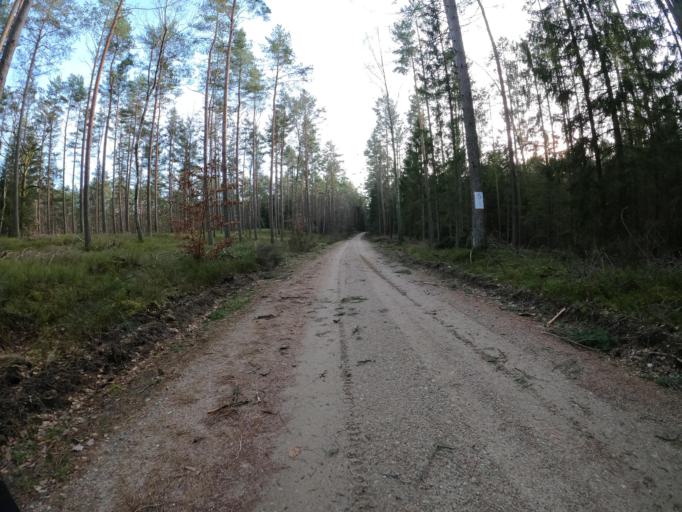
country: PL
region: West Pomeranian Voivodeship
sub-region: Powiat koszalinski
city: Polanow
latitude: 54.1494
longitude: 16.6762
